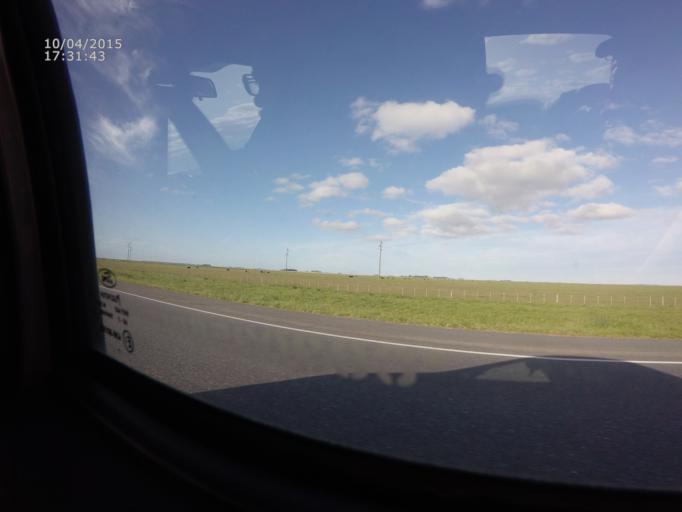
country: AR
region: Buenos Aires
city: Maipu
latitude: -36.9674
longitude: -57.8649
